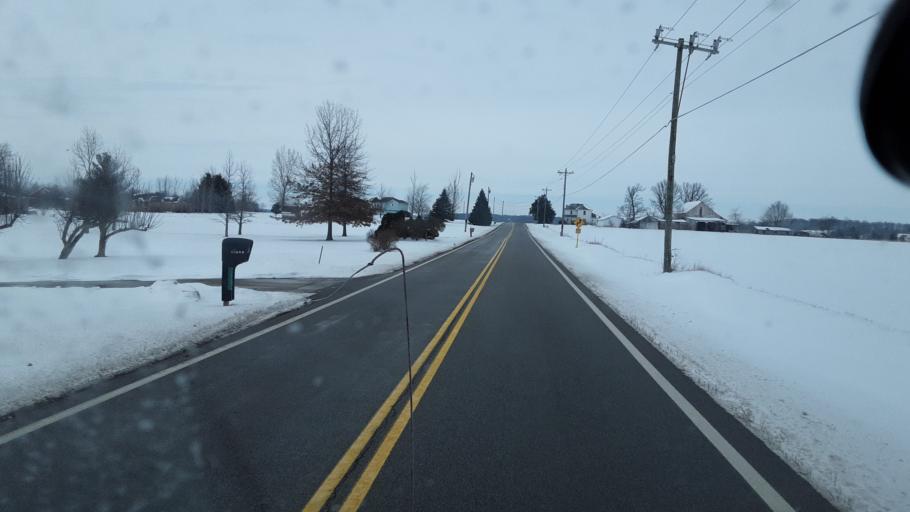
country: US
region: Ohio
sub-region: Union County
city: Marysville
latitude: 40.1580
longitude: -83.3482
